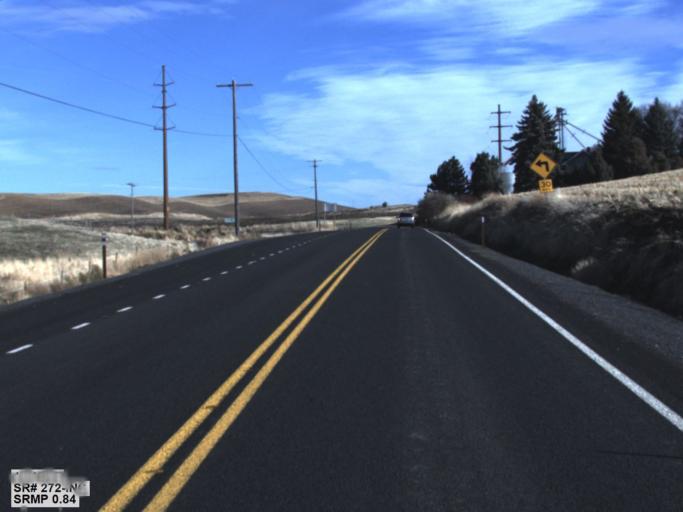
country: US
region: Washington
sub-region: Whitman County
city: Colfax
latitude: 46.8852
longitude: -117.3494
